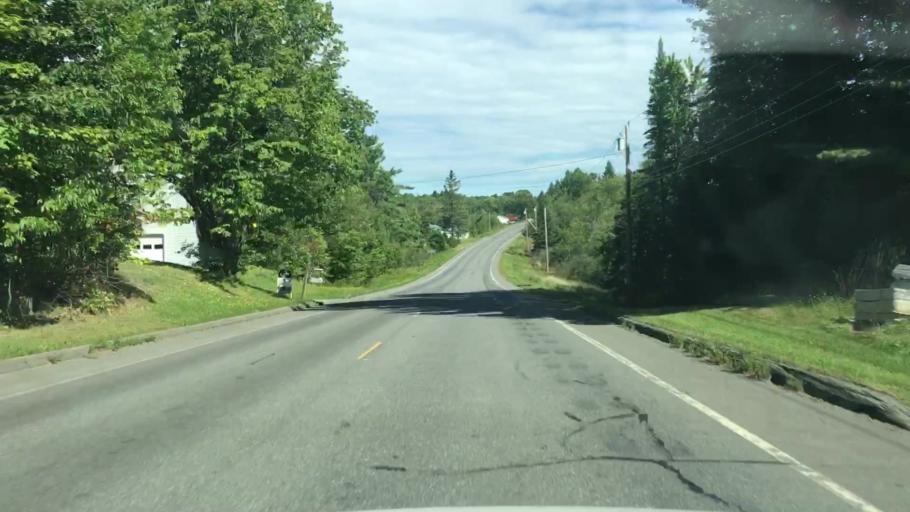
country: US
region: Maine
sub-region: Penobscot County
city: Dexter
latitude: 45.0790
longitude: -69.2305
